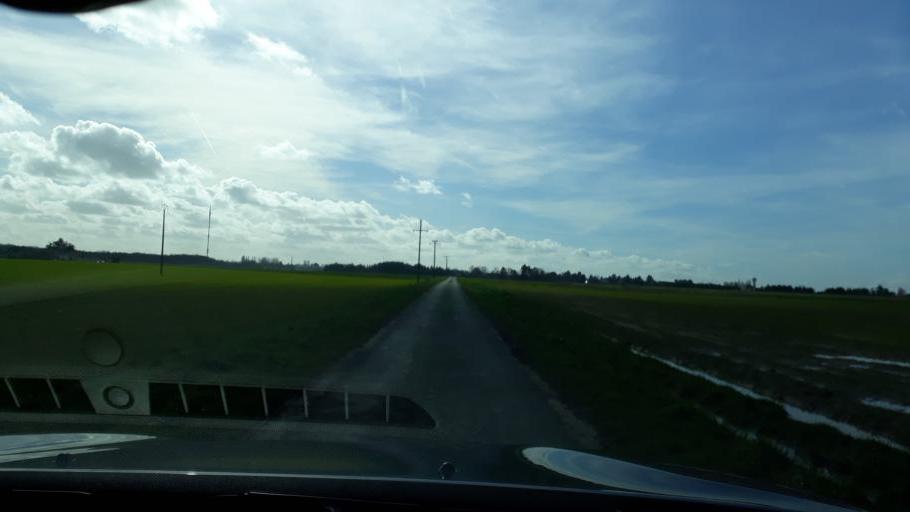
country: FR
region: Centre
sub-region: Departement du Loiret
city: Trainou
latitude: 47.9864
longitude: 2.1158
